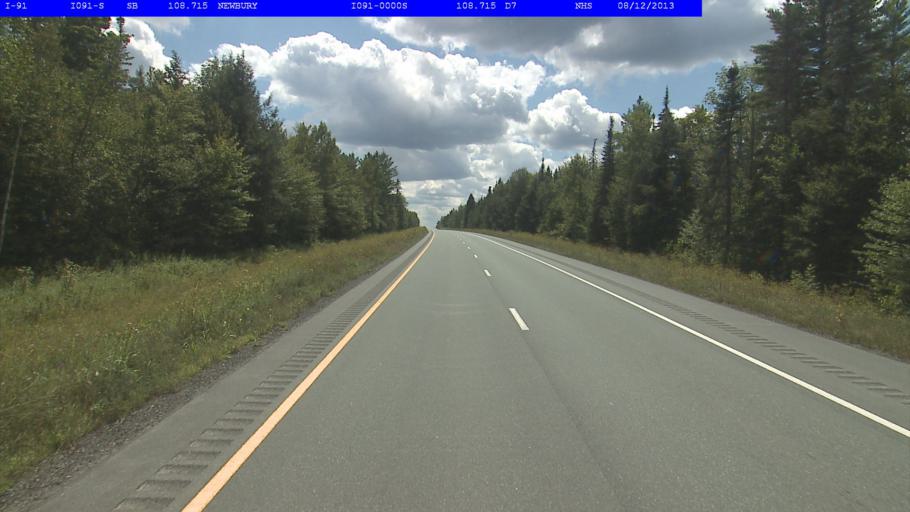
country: US
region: New Hampshire
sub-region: Grafton County
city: Woodsville
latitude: 44.1390
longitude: -72.1028
